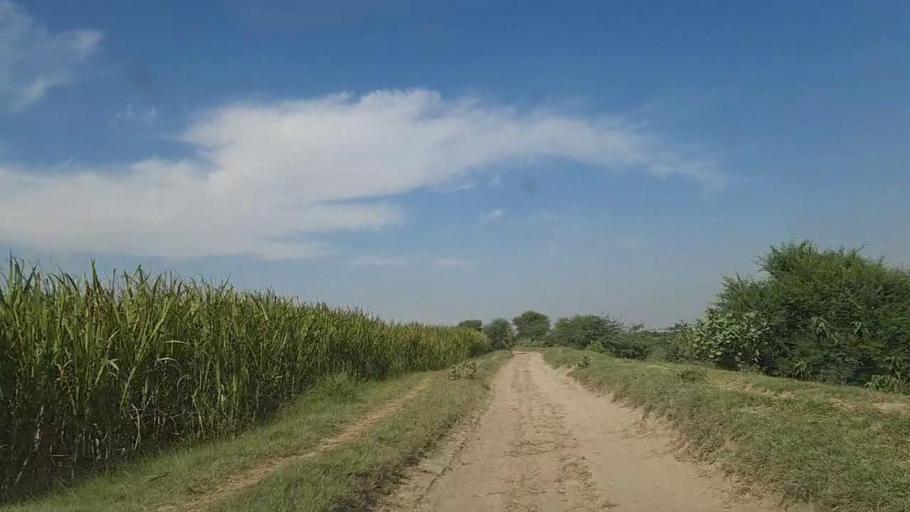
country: PK
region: Sindh
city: Mirpur Batoro
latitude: 24.8130
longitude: 68.2655
